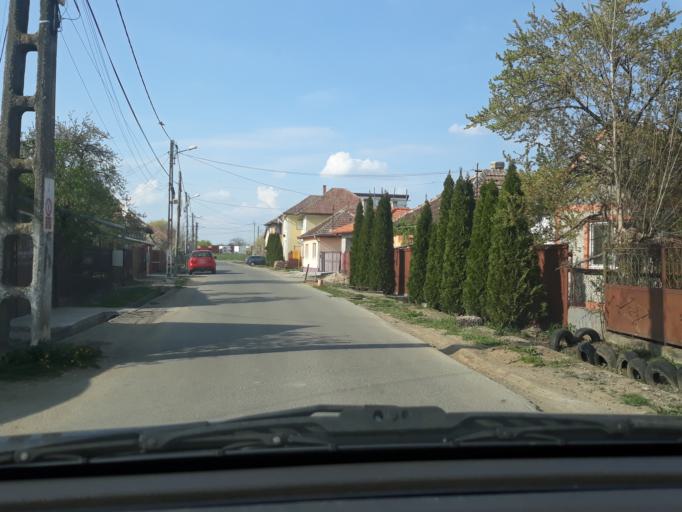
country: RO
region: Bihor
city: Margita
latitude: 47.3482
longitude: 22.3287
